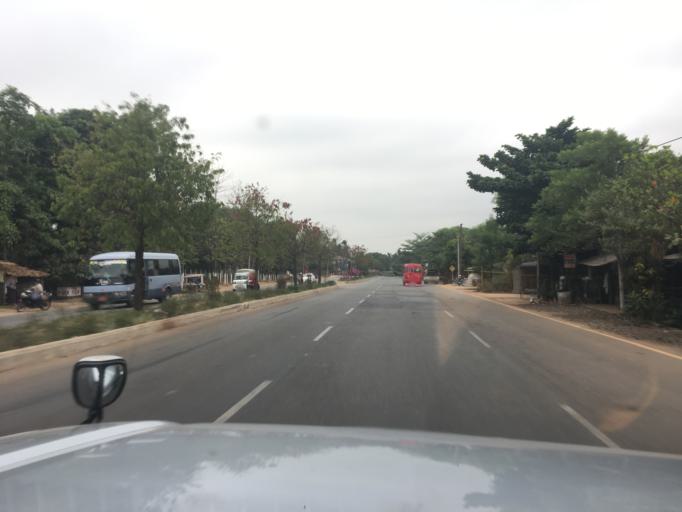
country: MM
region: Bago
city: Thanatpin
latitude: 17.1824
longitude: 96.3806
